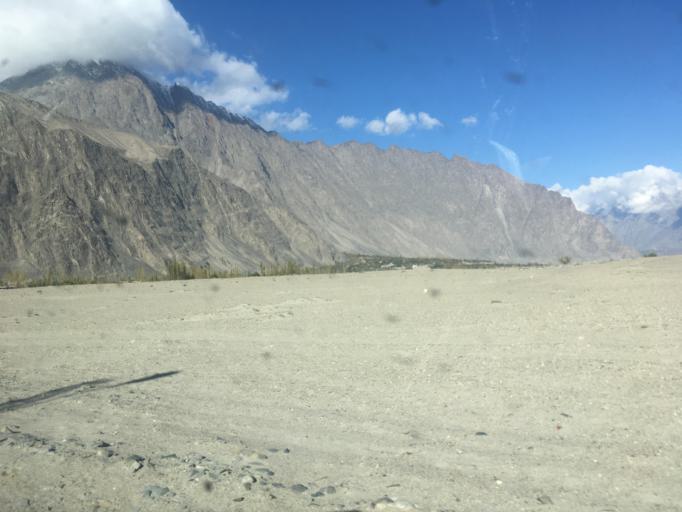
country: PK
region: Gilgit-Baltistan
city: Skardu
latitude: 35.3563
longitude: 75.5248
